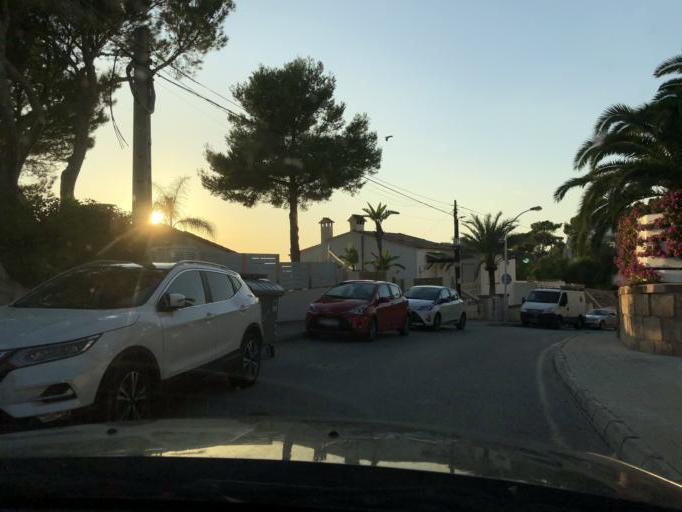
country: ES
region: Balearic Islands
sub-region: Illes Balears
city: Santa Ponsa
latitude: 39.5275
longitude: 2.4725
